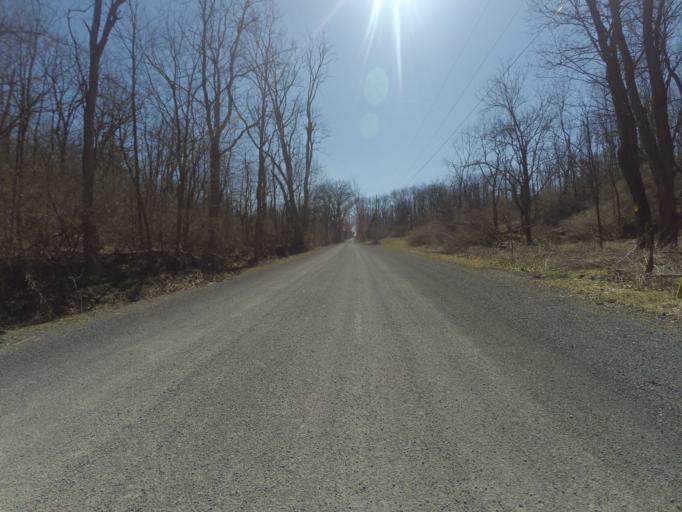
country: US
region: Pennsylvania
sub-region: Centre County
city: Bellefonte
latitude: 40.8922
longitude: -77.8313
